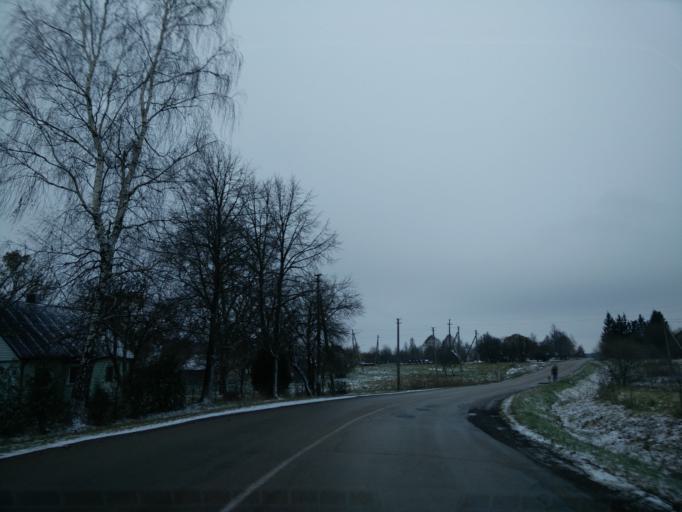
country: LT
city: Ariogala
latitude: 55.3874
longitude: 23.3430
